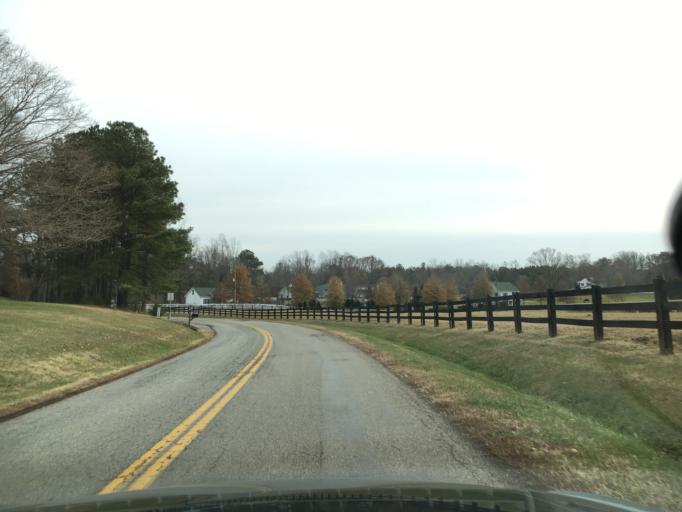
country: US
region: Virginia
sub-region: Henrico County
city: Wyndham
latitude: 37.7304
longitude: -77.6996
